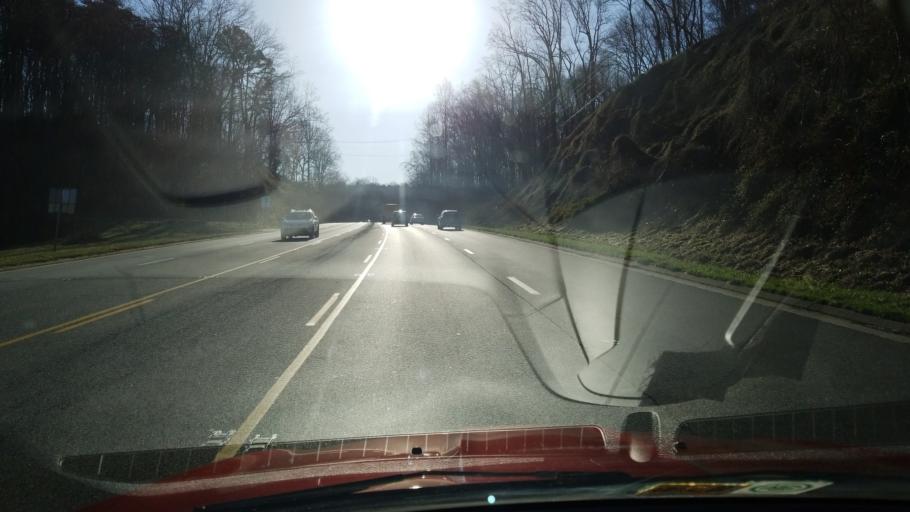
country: US
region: Virginia
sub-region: Roanoke County
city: Narrows
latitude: 37.1133
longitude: -79.9520
